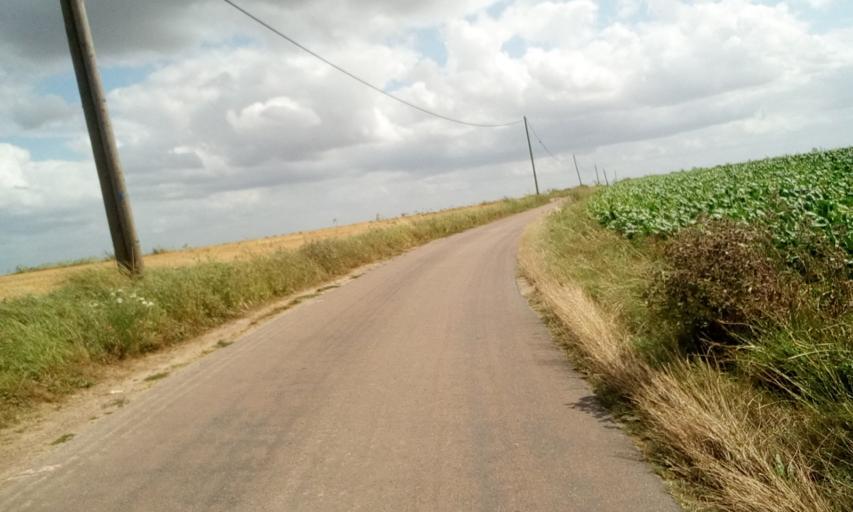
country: FR
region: Lower Normandy
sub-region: Departement du Calvados
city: Ver-sur-Mer
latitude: 49.3282
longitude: -0.5245
